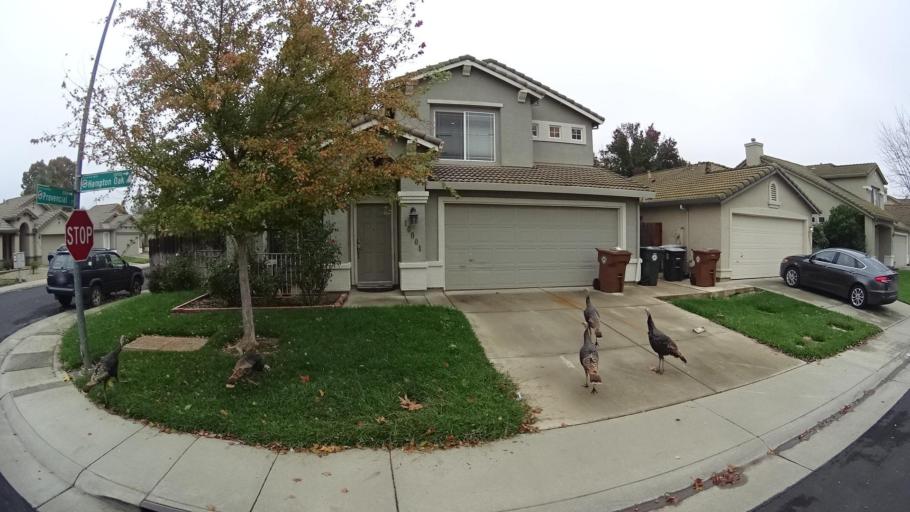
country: US
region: California
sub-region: Sacramento County
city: Elk Grove
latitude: 38.3940
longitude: -121.3615
